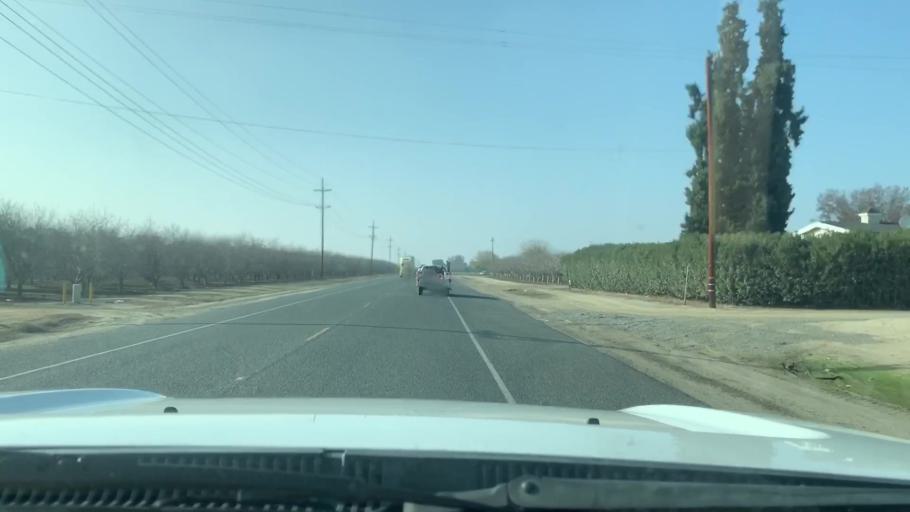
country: US
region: California
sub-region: Kern County
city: Wasco
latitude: 35.6015
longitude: -119.3713
